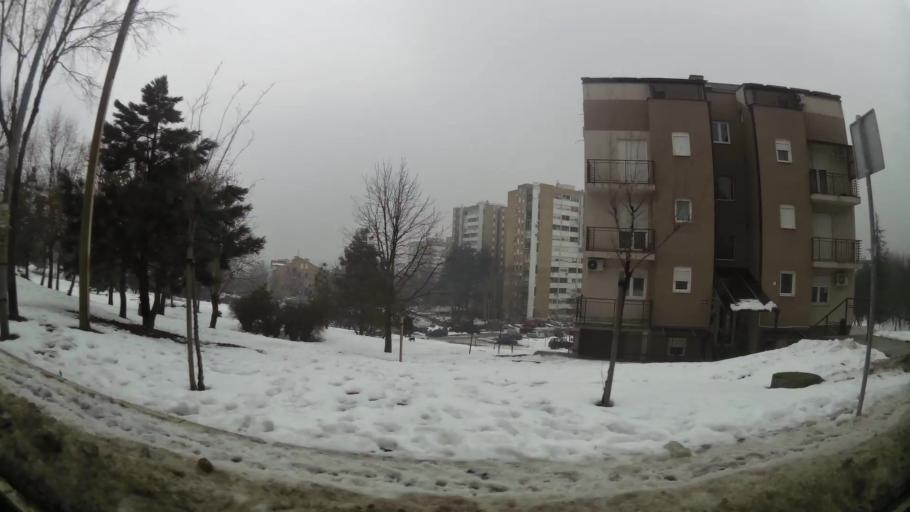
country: RS
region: Central Serbia
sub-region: Belgrade
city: Zvezdara
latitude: 44.7864
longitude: 20.5287
